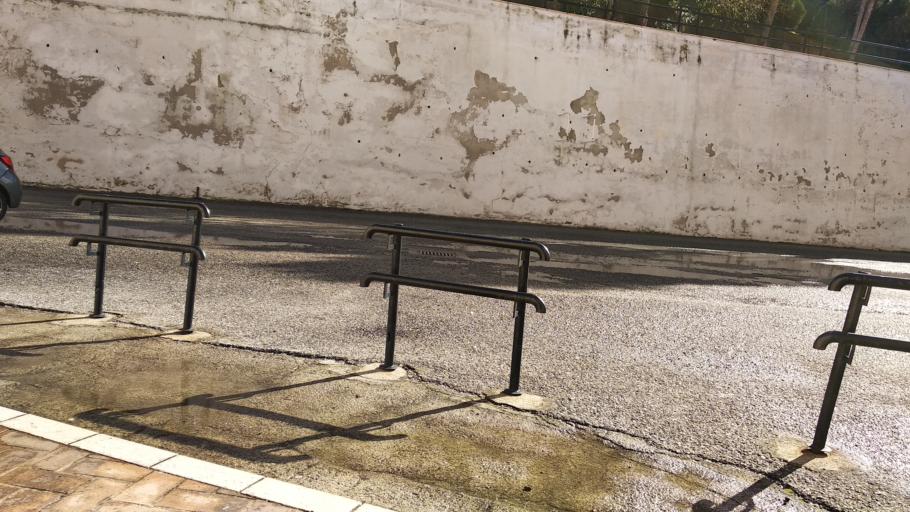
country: IT
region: Calabria
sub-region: Provincia di Reggio Calabria
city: Reggio Calabria
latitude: 38.1105
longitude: 15.6567
